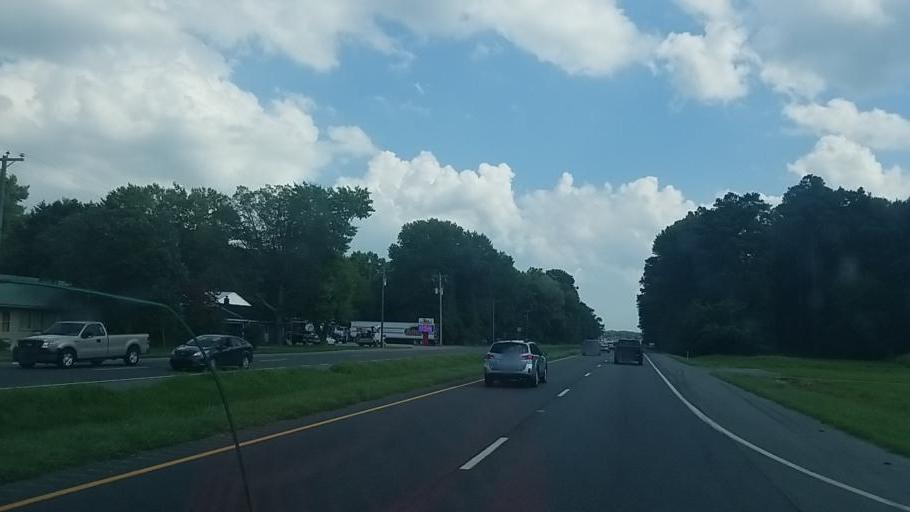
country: US
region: Delaware
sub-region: Sussex County
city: Millsboro
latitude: 38.5304
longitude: -75.2494
